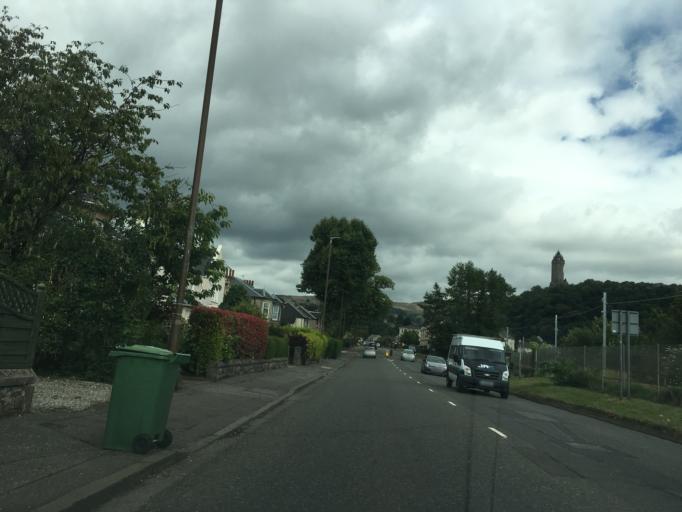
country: GB
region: Scotland
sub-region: Stirling
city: Stirling
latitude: 56.1340
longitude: -3.9293
